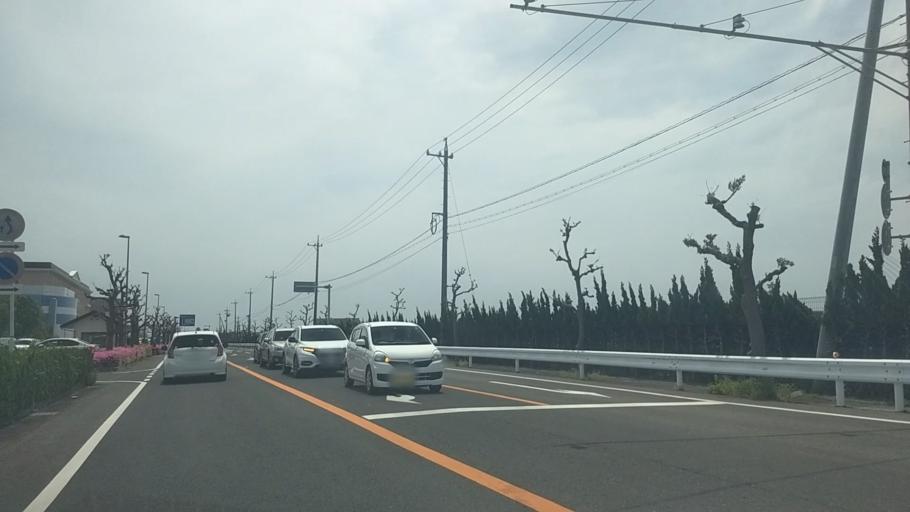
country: JP
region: Shizuoka
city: Kosai-shi
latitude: 34.7016
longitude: 137.5712
